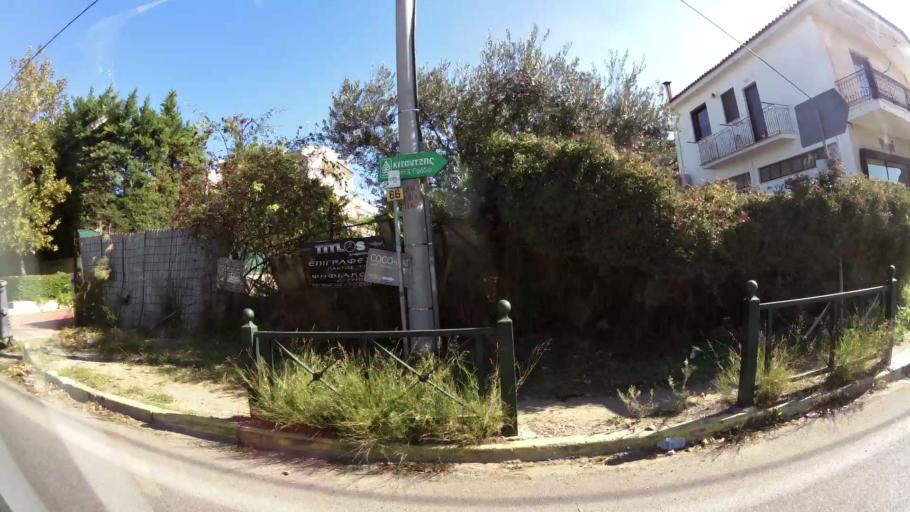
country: GR
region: Attica
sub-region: Nomarchia Athinas
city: Lykovrysi
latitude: 38.0781
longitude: 23.7944
